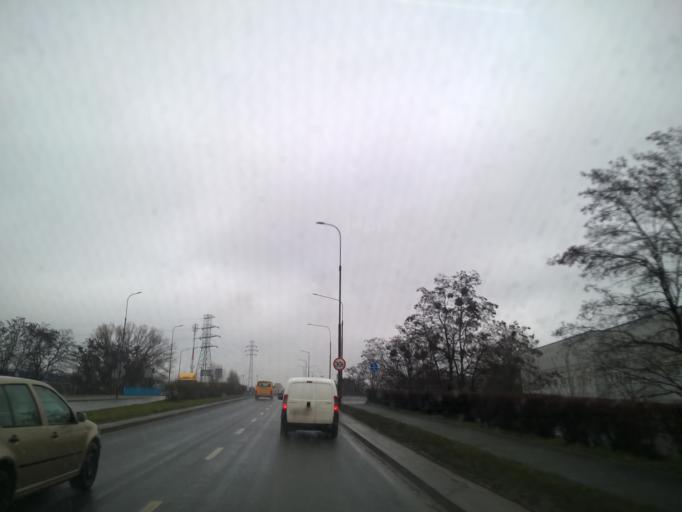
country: PL
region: Lower Silesian Voivodeship
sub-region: Powiat wroclawski
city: Wroclaw
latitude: 51.0851
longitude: 17.0653
